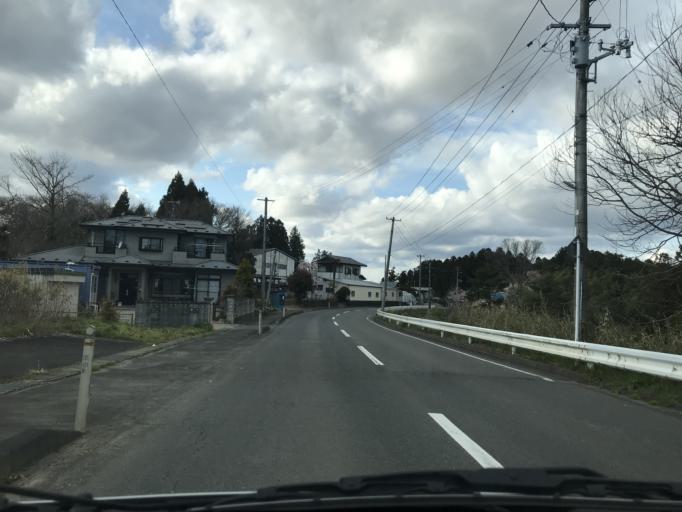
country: JP
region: Miyagi
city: Wakuya
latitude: 38.6389
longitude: 141.2135
